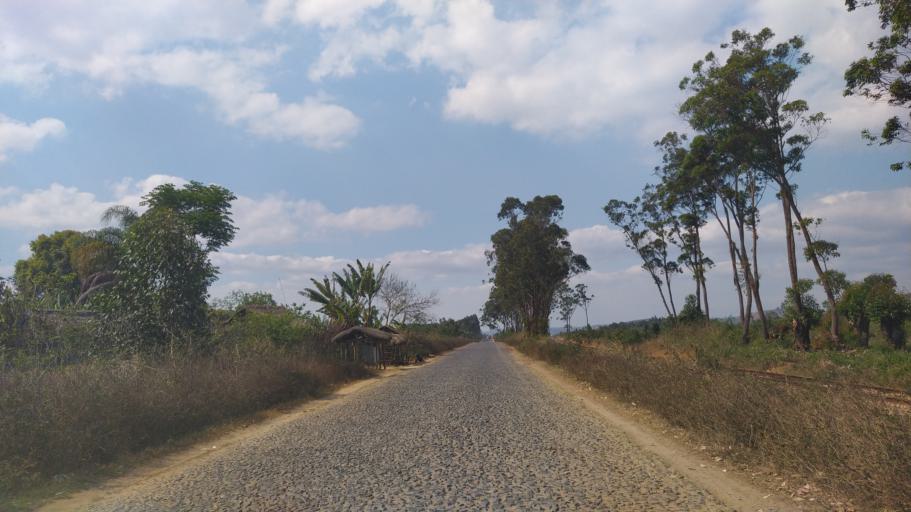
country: MG
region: Alaotra Mangoro
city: Moramanga
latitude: -18.7782
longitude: 48.2490
